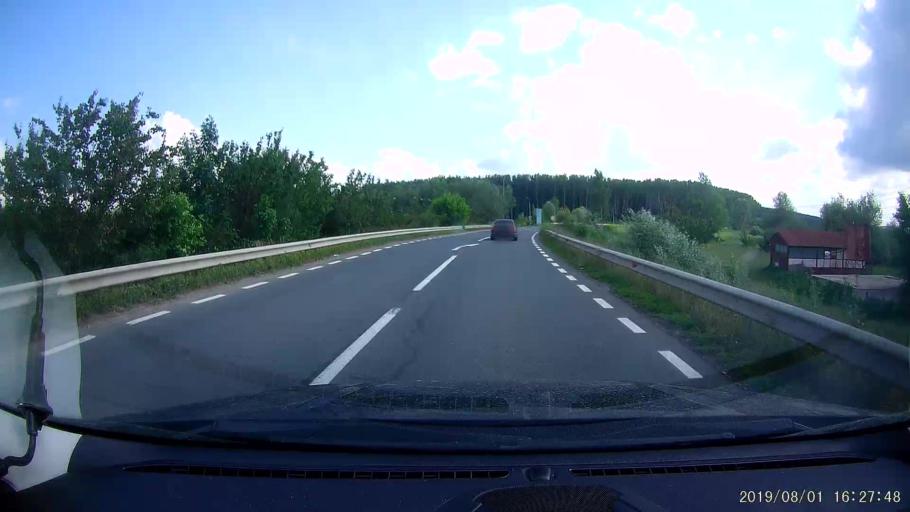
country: RO
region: Calarasi
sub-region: Municipiul Calarasi
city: Calarasi
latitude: 44.1585
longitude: 27.3171
